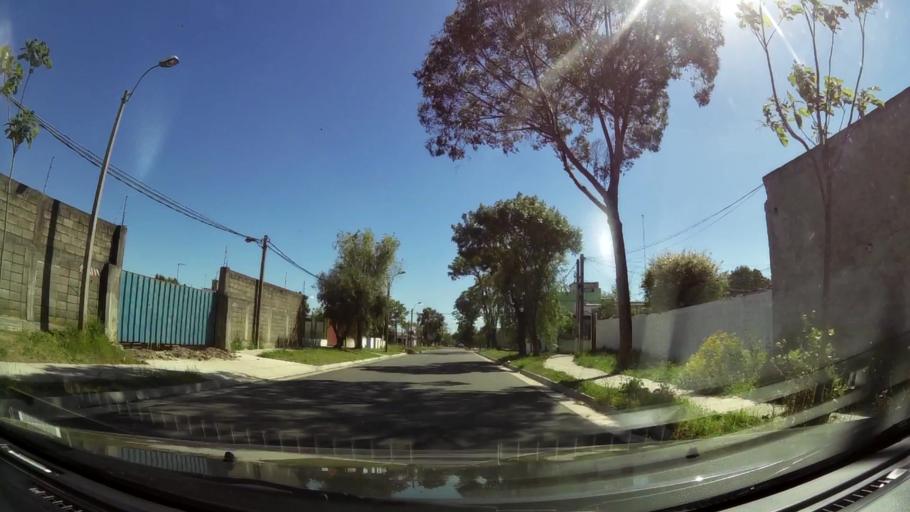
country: UY
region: Montevideo
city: Montevideo
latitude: -34.8656
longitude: -56.1274
